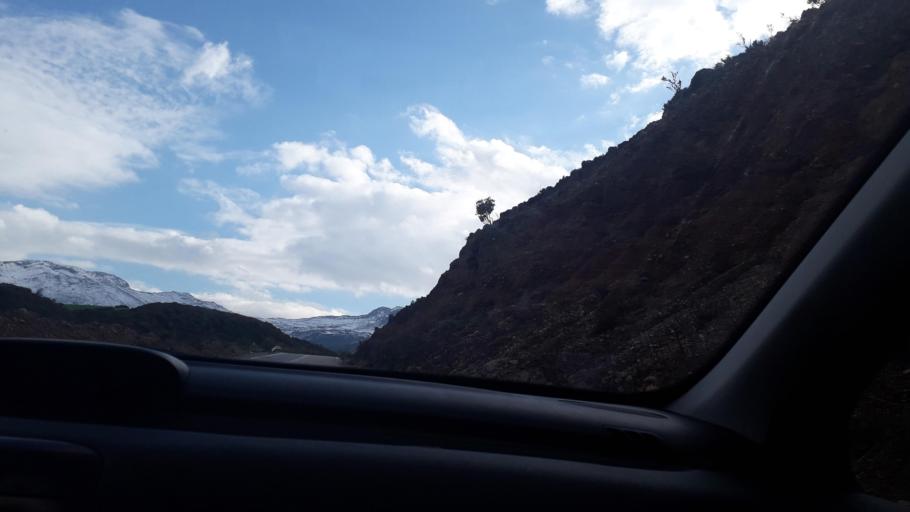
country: GR
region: Crete
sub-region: Nomos Rethymnis
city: Agia Foteini
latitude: 35.2813
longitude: 24.5619
